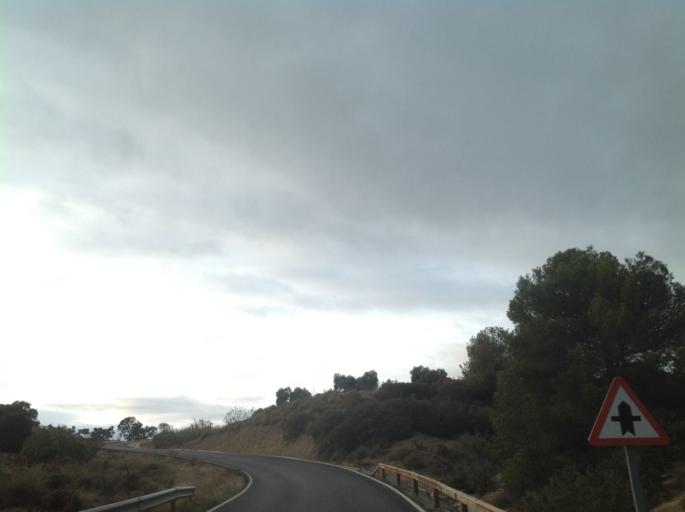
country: ES
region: Andalusia
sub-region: Provincia de Malaga
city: Ardales
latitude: 36.9137
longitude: -4.8055
